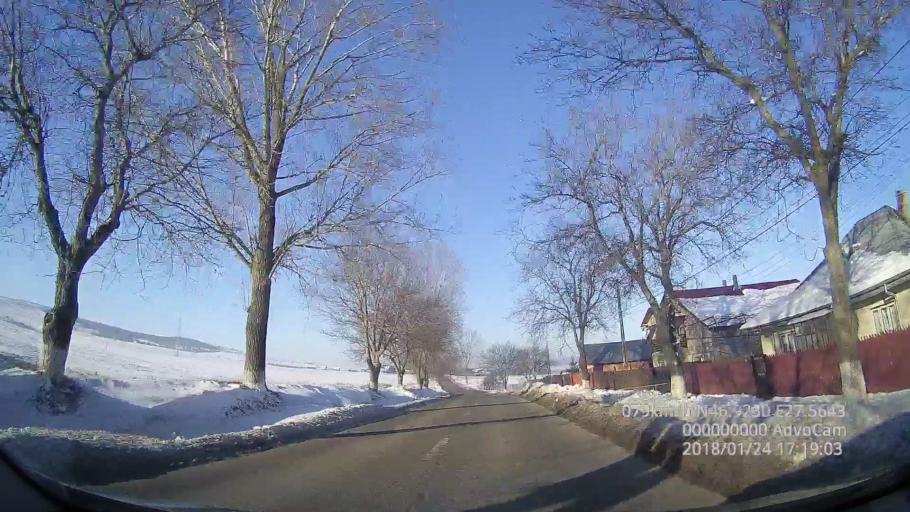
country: RO
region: Iasi
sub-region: Comuna Scanteia
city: Scanteia
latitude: 46.9236
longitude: 27.5643
